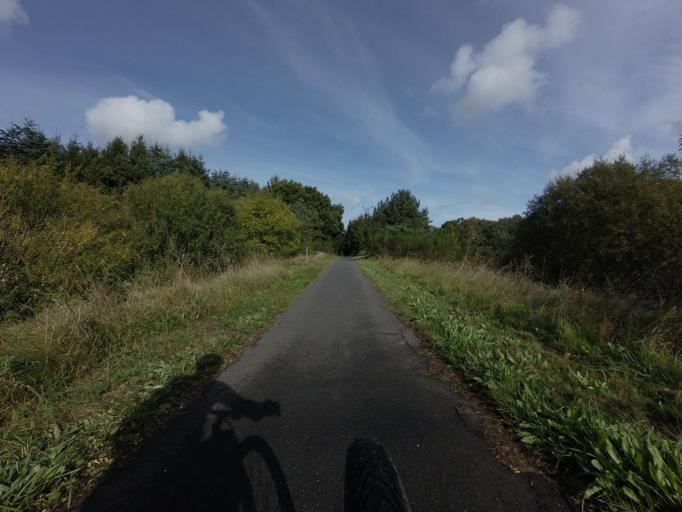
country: DK
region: Central Jutland
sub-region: Viborg Kommune
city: Bjerringbro
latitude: 56.4643
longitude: 9.5893
